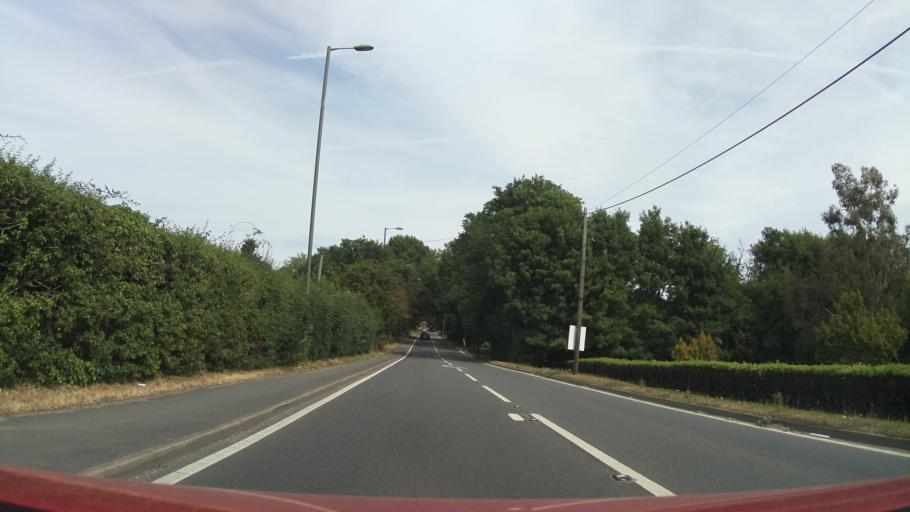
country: GB
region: England
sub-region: Surrey
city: Salfords
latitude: 51.1800
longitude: -0.1952
